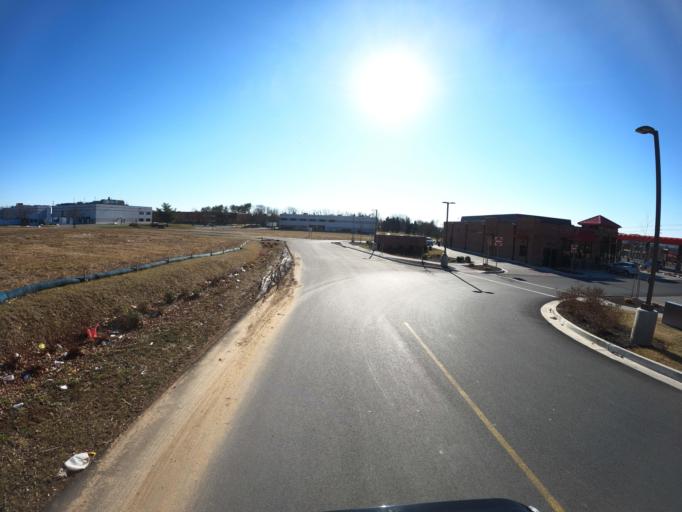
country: US
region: Maryland
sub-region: Frederick County
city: Ballenger Creek
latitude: 39.3694
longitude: -77.4116
